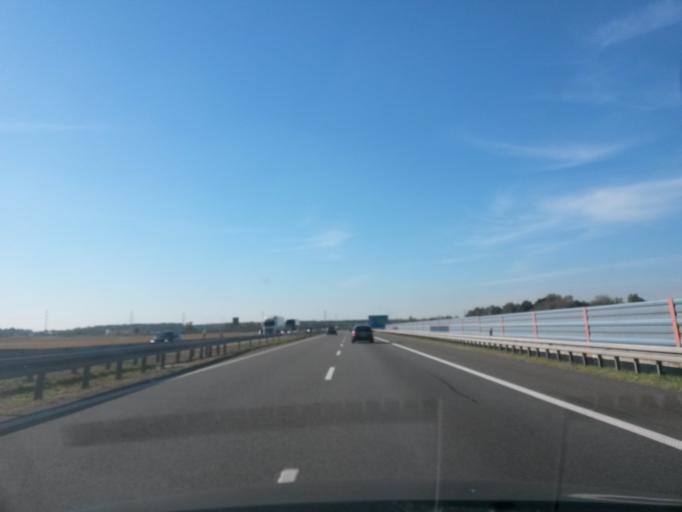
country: PL
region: Opole Voivodeship
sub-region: Powiat krapkowicki
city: Krapkowice
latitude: 50.5256
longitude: 17.9291
